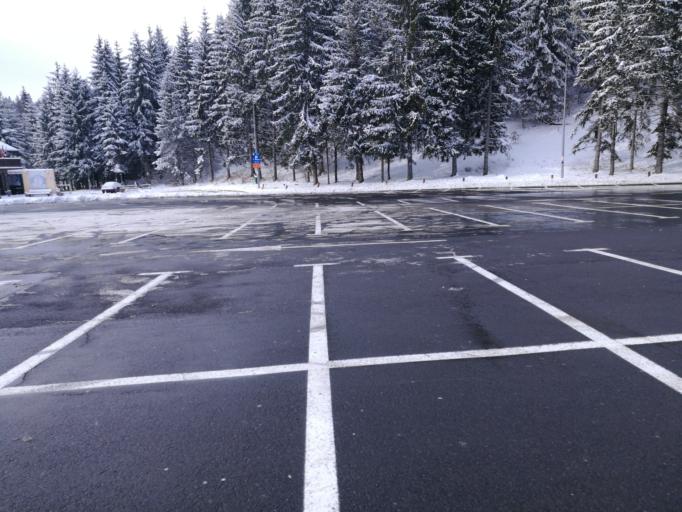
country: RO
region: Brasov
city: Brasov
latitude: 45.5954
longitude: 25.5530
